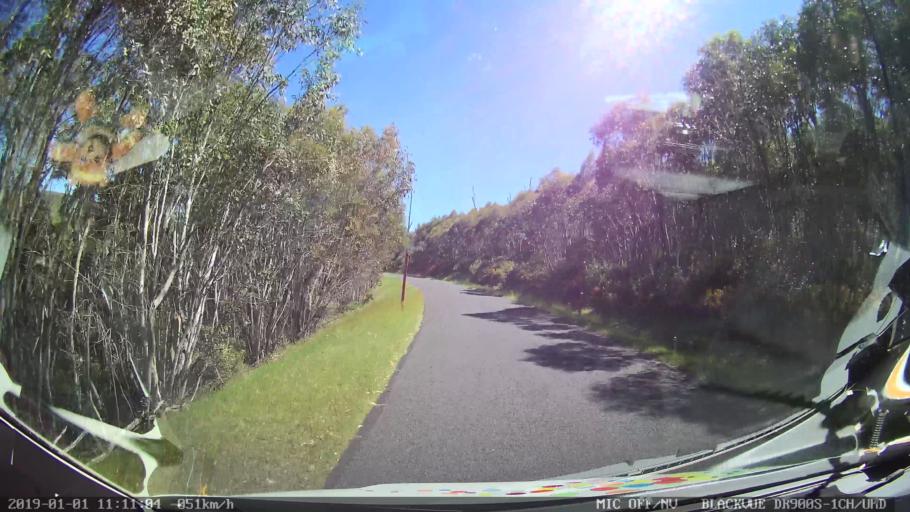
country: AU
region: New South Wales
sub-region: Snowy River
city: Jindabyne
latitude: -35.9646
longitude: 148.4010
